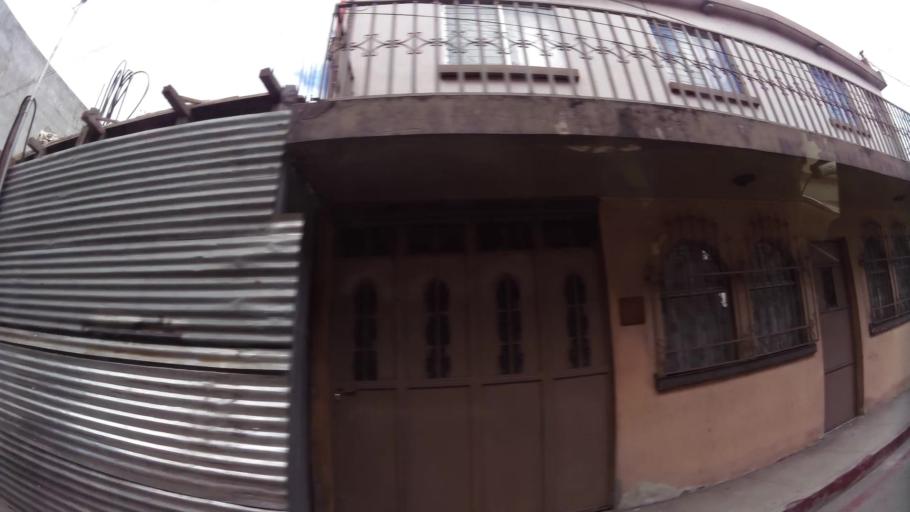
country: GT
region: Quetzaltenango
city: Salcaja
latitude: 14.8807
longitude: -91.4580
